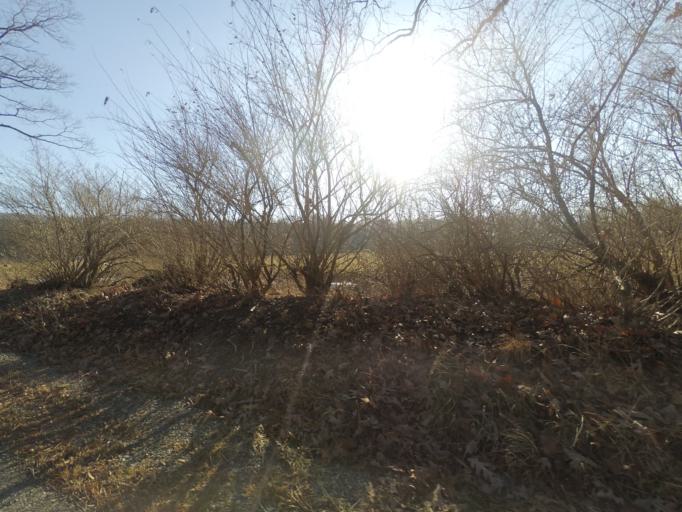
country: US
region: Pennsylvania
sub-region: Centre County
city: Boalsburg
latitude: 40.7683
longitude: -77.8258
